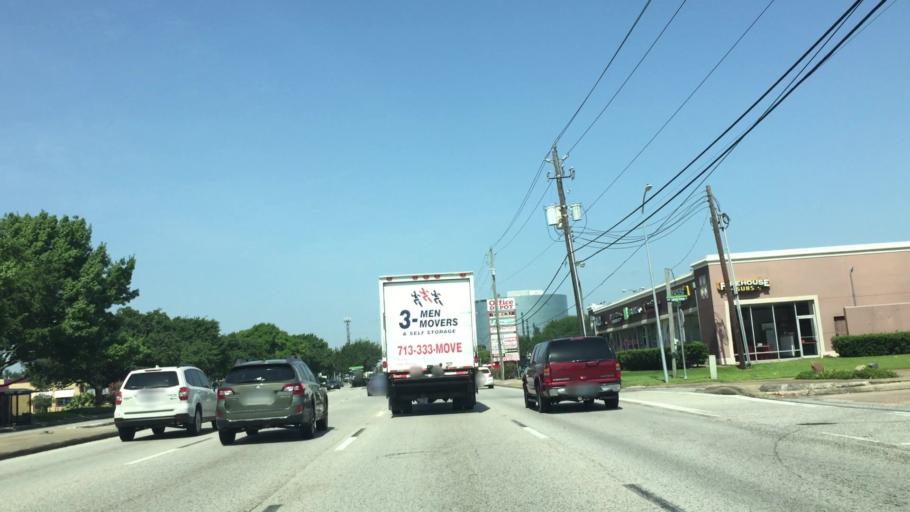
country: US
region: Texas
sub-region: Harris County
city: Bunker Hill Village
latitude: 29.7369
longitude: -95.5684
